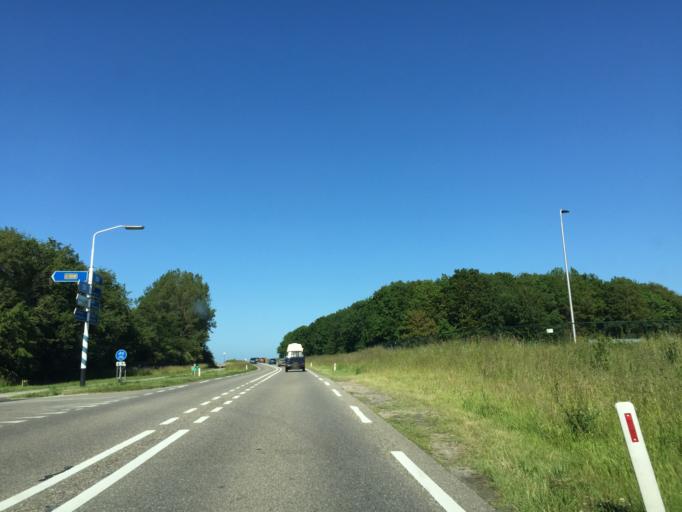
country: NL
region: Zeeland
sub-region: Schouwen-Duiveland
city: Burgh
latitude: 51.6880
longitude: 3.7377
